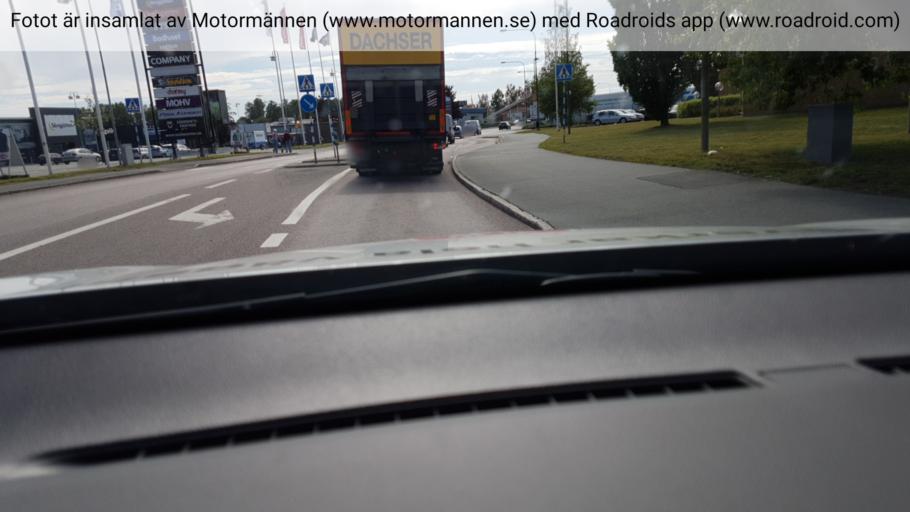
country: SE
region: Joenkoeping
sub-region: Jonkopings Kommun
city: Jonkoping
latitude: 57.7628
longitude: 14.1844
